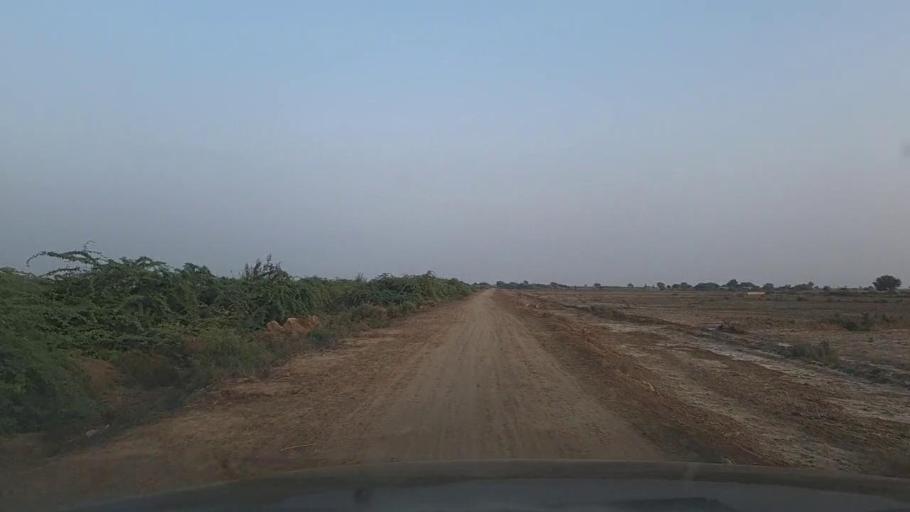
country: PK
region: Sindh
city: Jati
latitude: 24.5415
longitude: 68.3982
